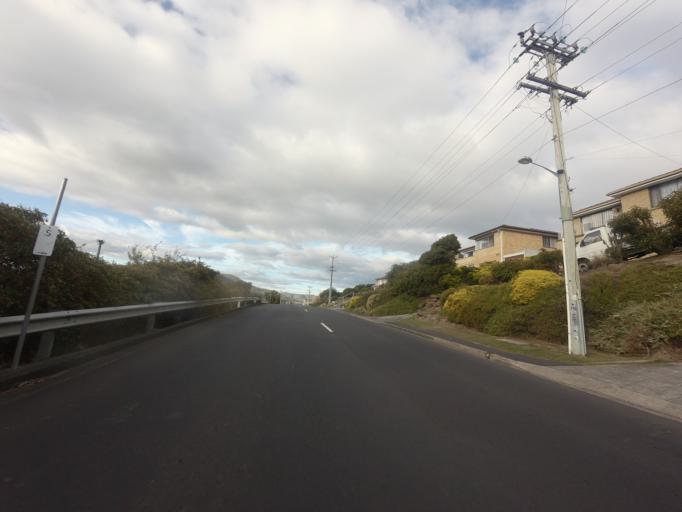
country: AU
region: Tasmania
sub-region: Glenorchy
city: Berriedale
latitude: -42.8235
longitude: 147.2555
